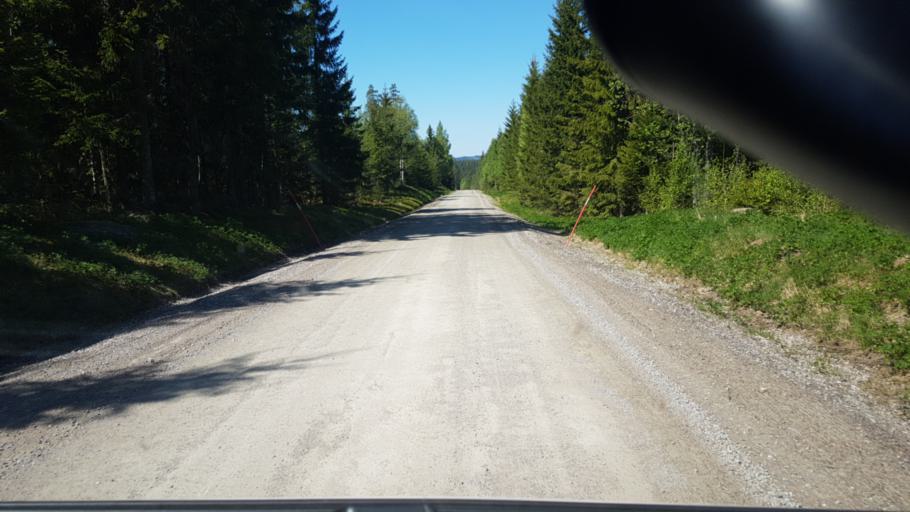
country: SE
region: Vaermland
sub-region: Arvika Kommun
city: Arvika
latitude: 59.8825
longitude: 12.6785
